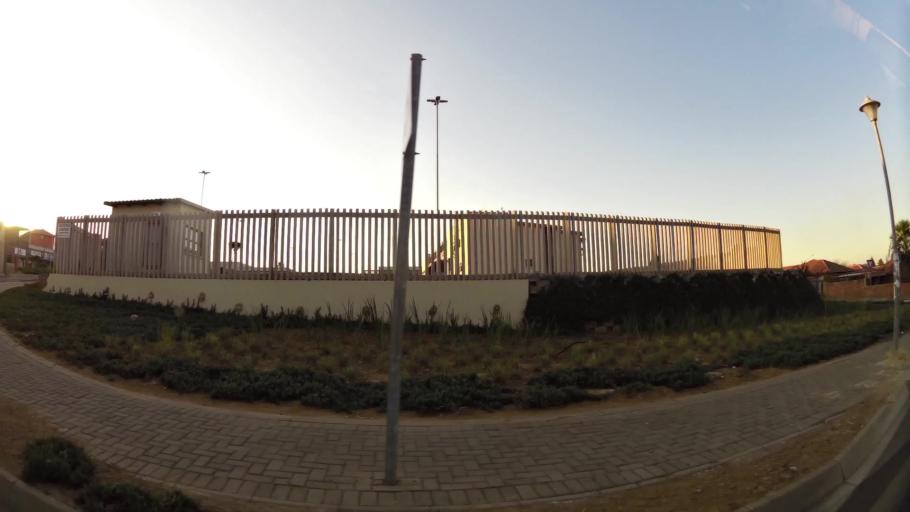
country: ZA
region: Gauteng
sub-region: City of Tshwane Metropolitan Municipality
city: Pretoria
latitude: -25.7480
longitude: 28.1143
